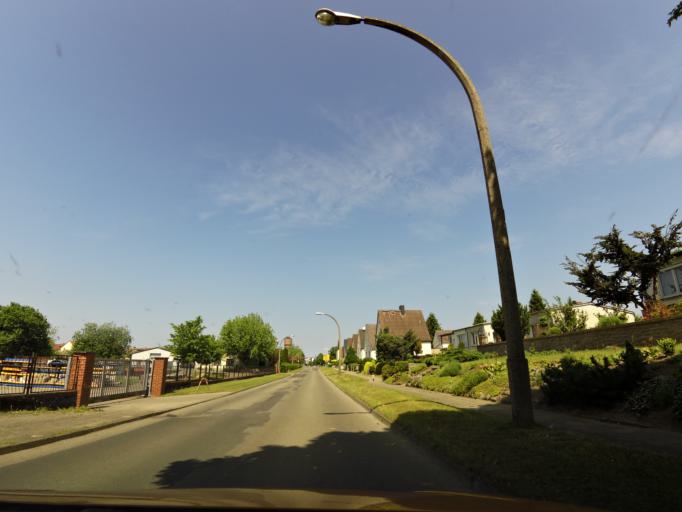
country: DE
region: Mecklenburg-Vorpommern
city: Parchim
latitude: 53.4240
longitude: 11.8641
